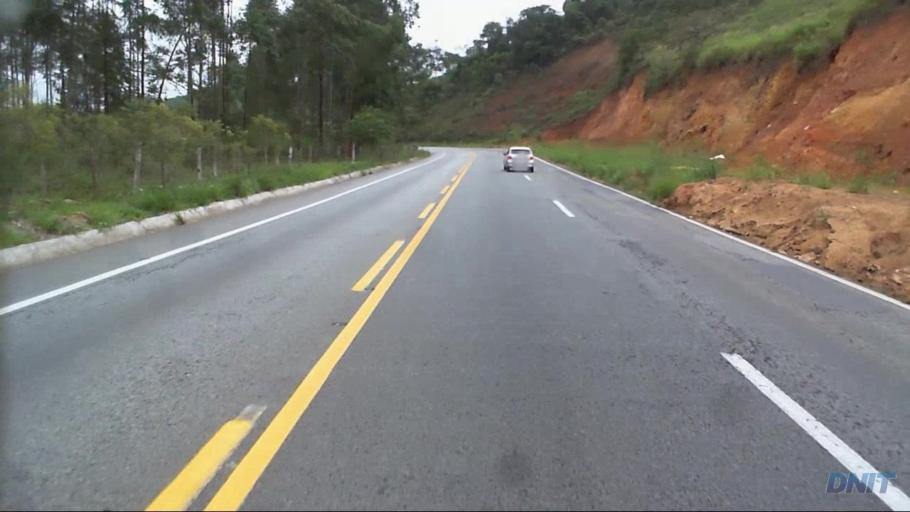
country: BR
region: Minas Gerais
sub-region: Nova Era
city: Nova Era
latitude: -19.6305
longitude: -42.8777
